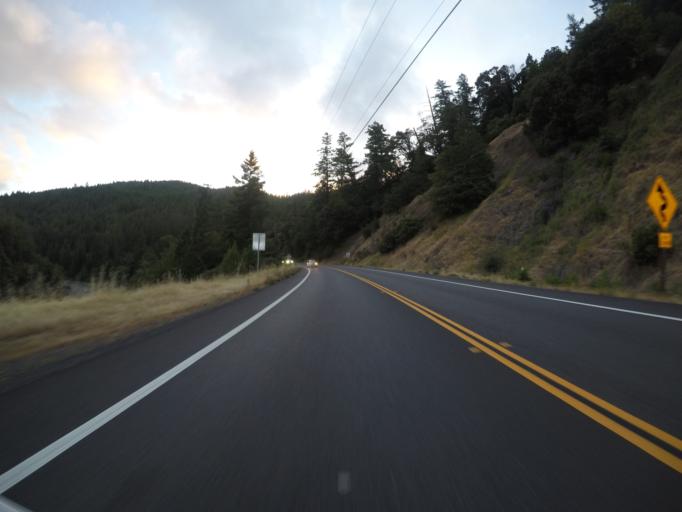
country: US
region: California
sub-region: Humboldt County
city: Redway
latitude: 40.0353
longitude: -123.7880
